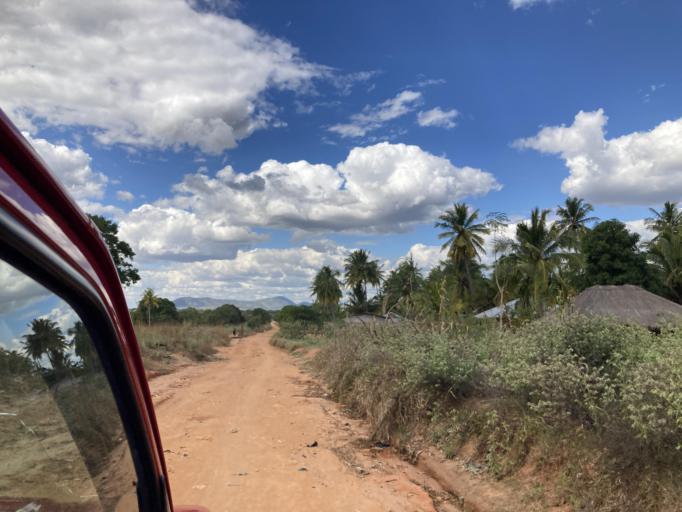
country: MZ
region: Cabo Delgado
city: Montepuez
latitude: -13.1266
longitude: 39.0363
